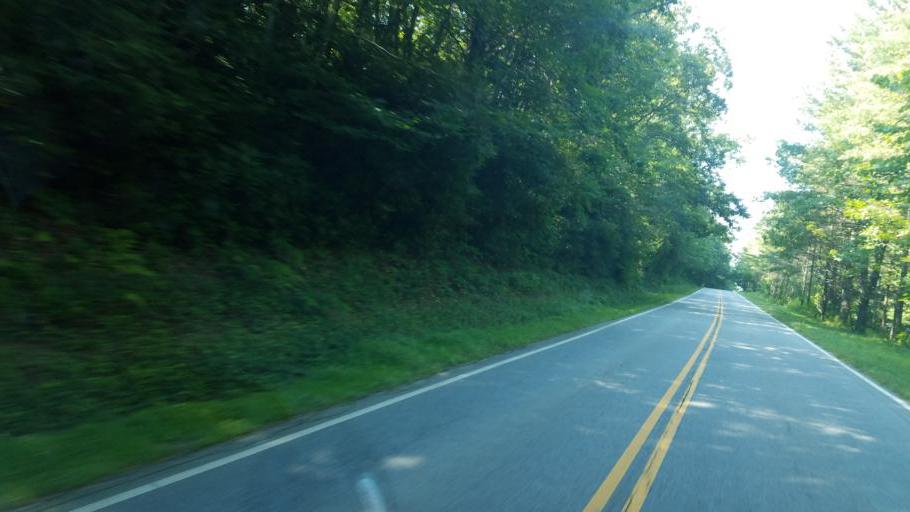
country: US
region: North Carolina
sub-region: Avery County
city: Newland
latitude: 35.9996
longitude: -81.8897
